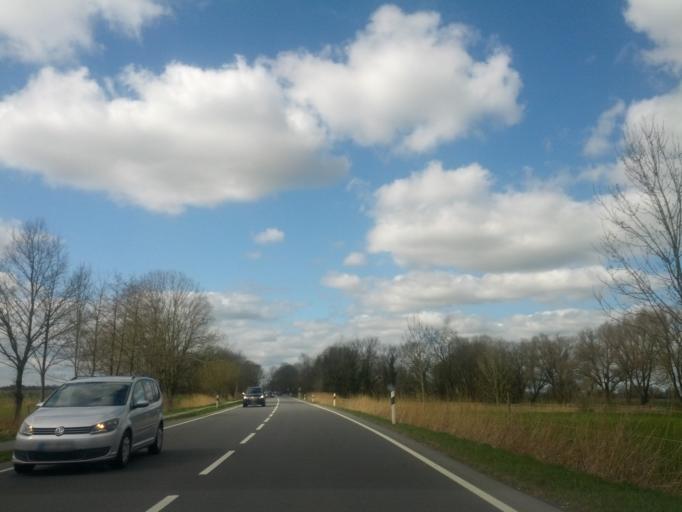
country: DE
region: Lower Saxony
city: Jever
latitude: 53.5792
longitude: 7.8564
